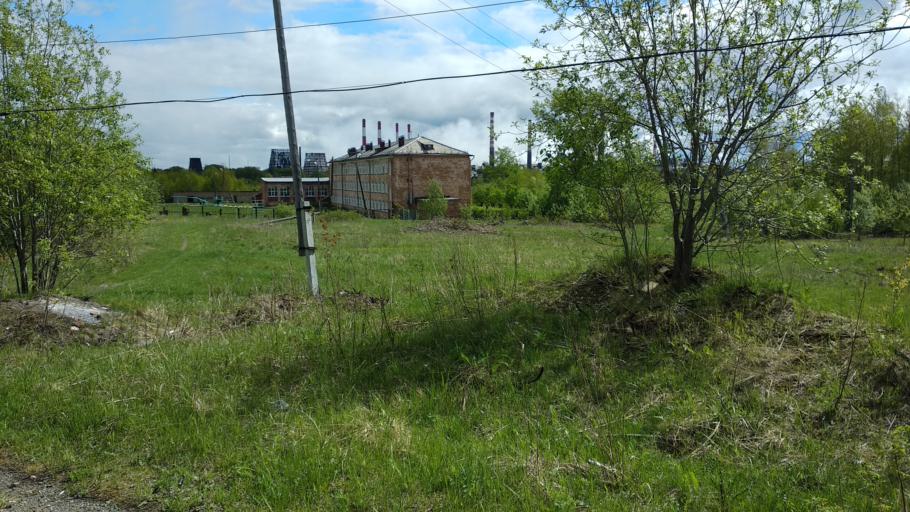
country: RU
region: Sverdlovsk
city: Krasnotur'insk
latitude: 59.7877
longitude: 60.1526
